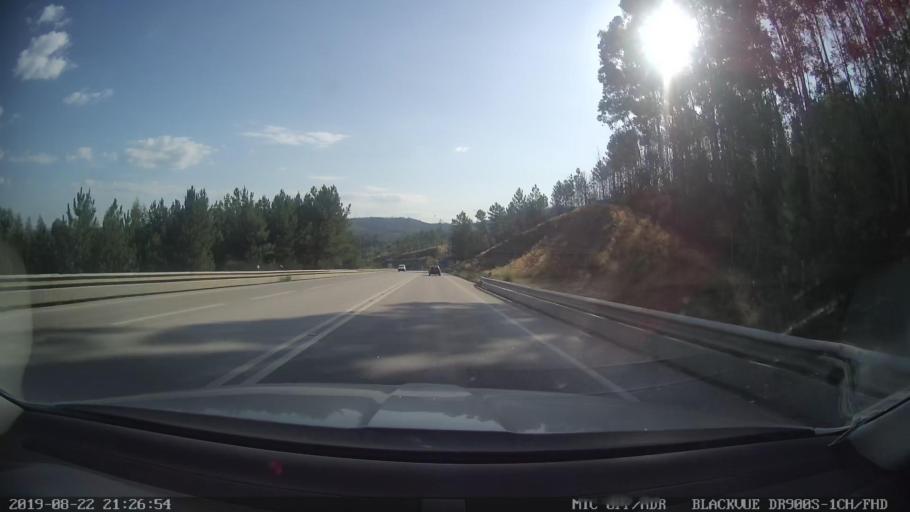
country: PT
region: Leiria
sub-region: Pedrogao Grande
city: Pedrogao Grande
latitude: 39.8717
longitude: -8.1223
